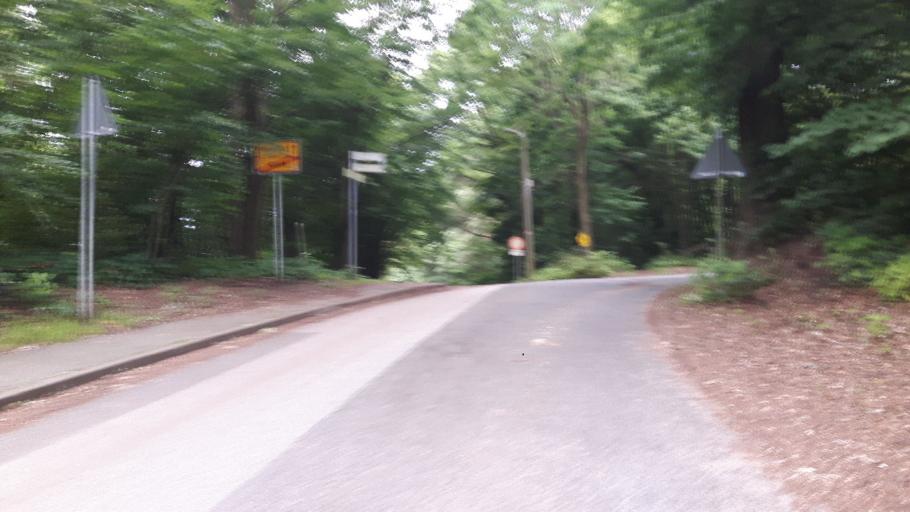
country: DE
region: Schleswig-Holstein
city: Ratekau
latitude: 53.9142
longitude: 10.7858
